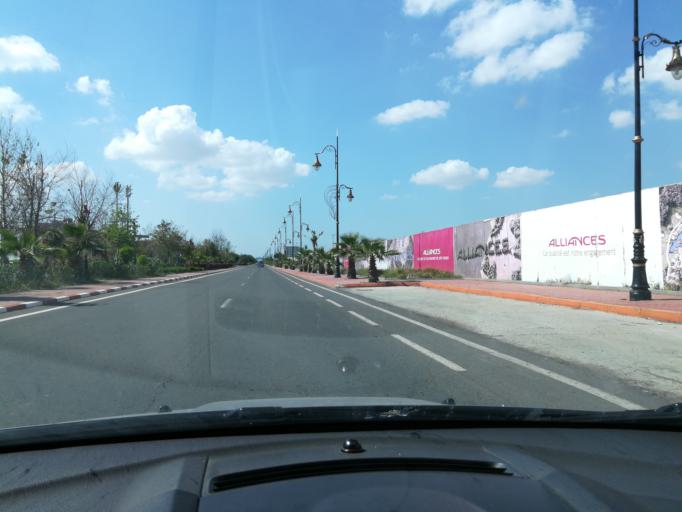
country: MA
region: Marrakech-Tensift-Al Haouz
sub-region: Marrakech
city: Marrakesh
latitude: 31.5849
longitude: -7.9863
